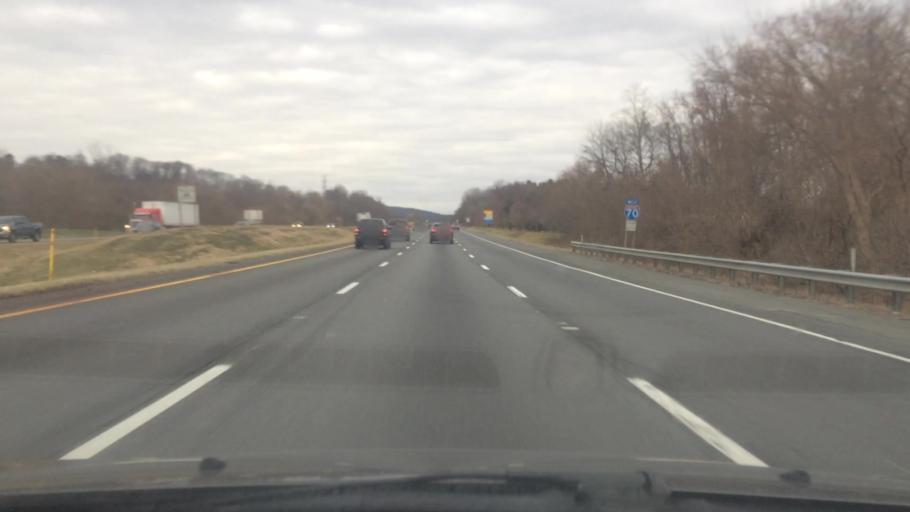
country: US
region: Maryland
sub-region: Frederick County
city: Myersville
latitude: 39.5001
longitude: -77.5735
